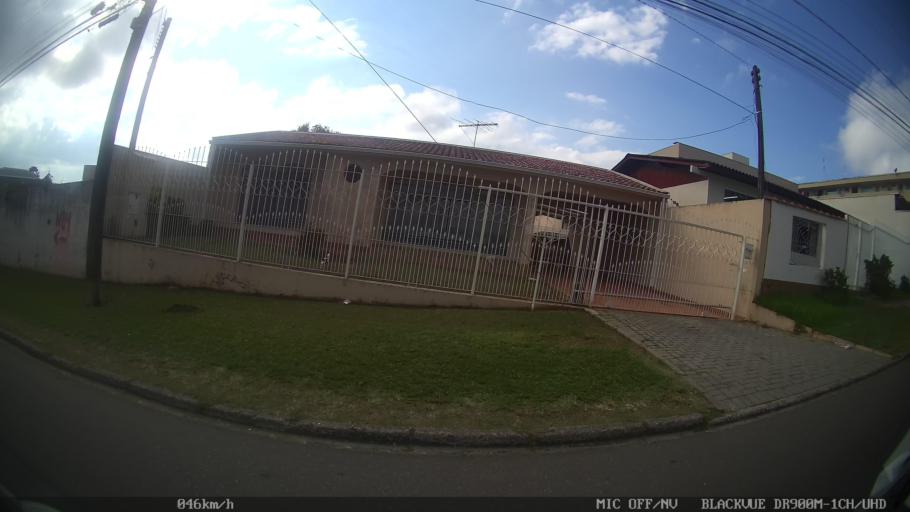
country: BR
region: Parana
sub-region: Pinhais
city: Pinhais
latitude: -25.4033
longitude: -49.1835
